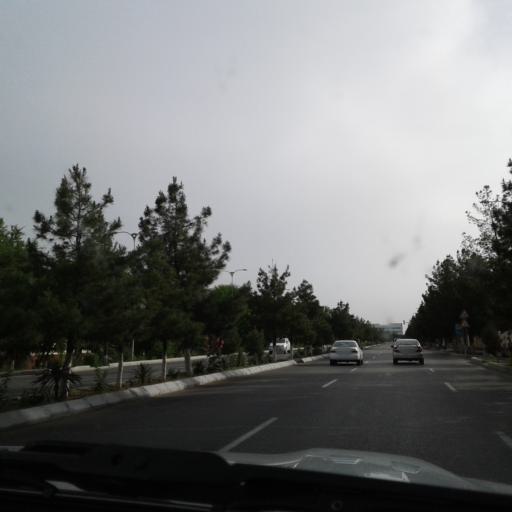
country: TM
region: Mary
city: Mary
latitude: 37.5882
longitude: 61.8653
